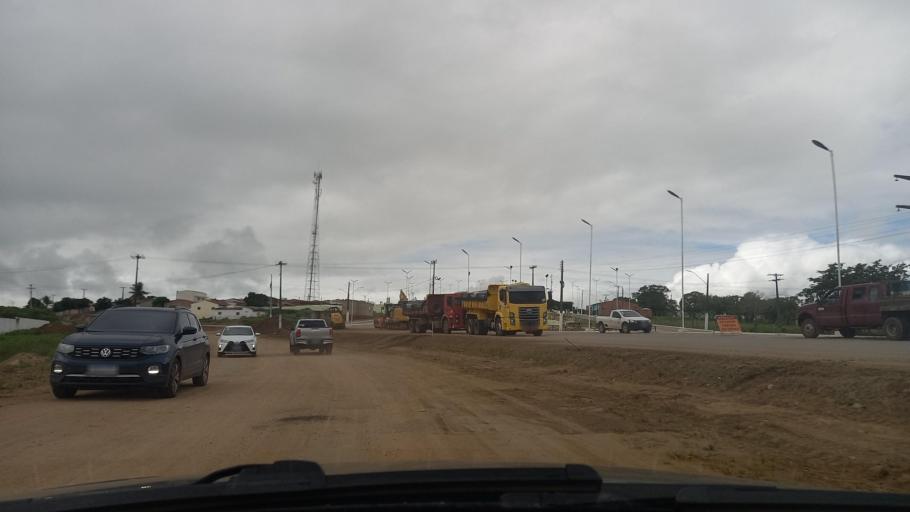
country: BR
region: Alagoas
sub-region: Batalha
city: Batalha
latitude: -9.6304
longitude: -37.2081
